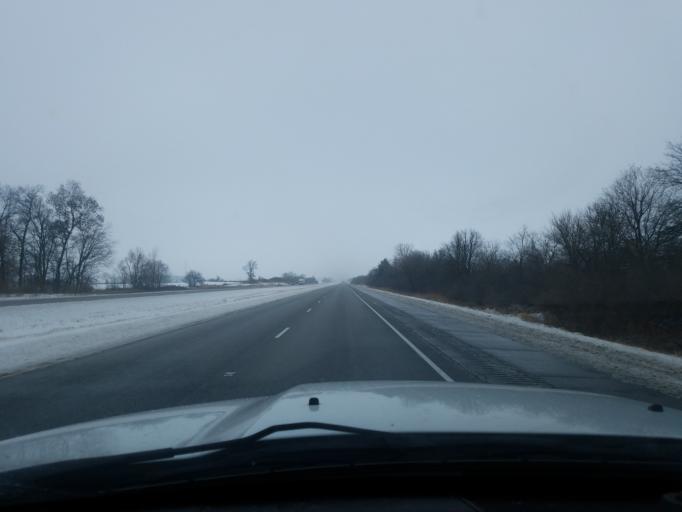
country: US
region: Indiana
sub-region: Fulton County
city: Rochester
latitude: 40.9712
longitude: -86.1680
